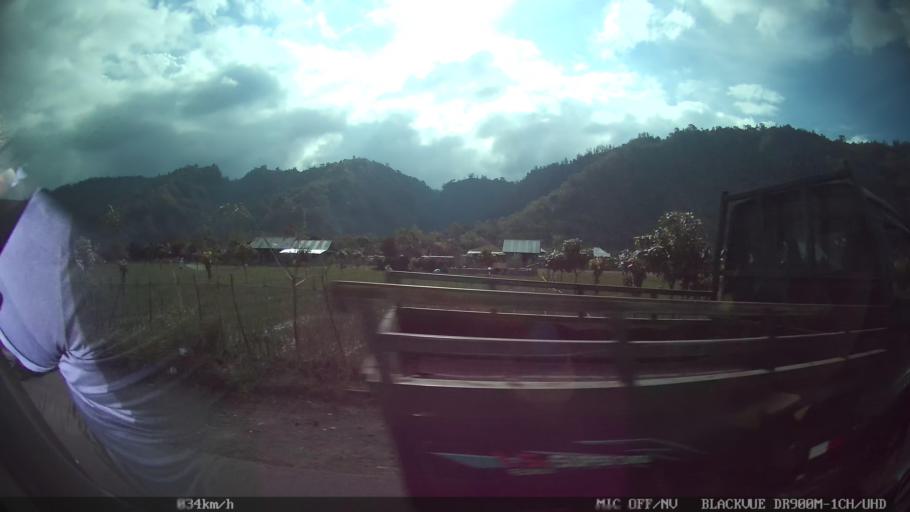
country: ID
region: Bali
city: Banjar Kedisan
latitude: -8.2257
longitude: 115.3596
